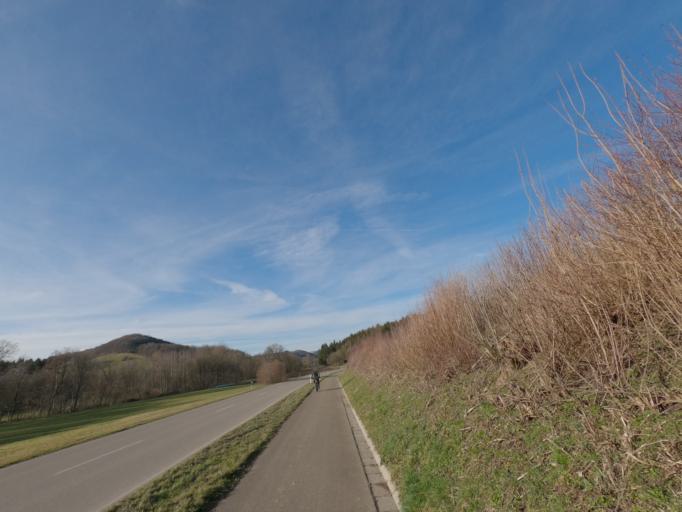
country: DE
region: Baden-Wuerttemberg
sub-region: Regierungsbezirk Stuttgart
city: Donzdorf
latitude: 48.6987
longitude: 9.8013
